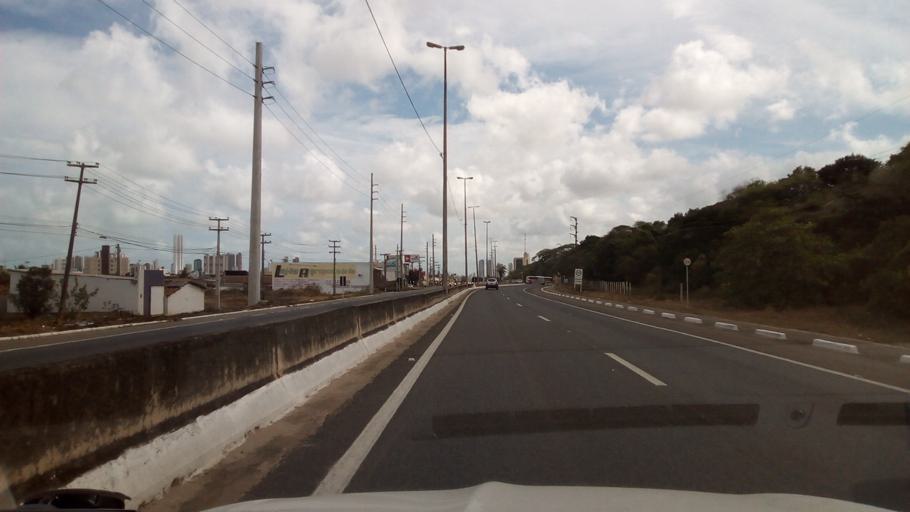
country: BR
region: Paraiba
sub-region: Joao Pessoa
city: Joao Pessoa
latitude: -7.0612
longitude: -34.8505
